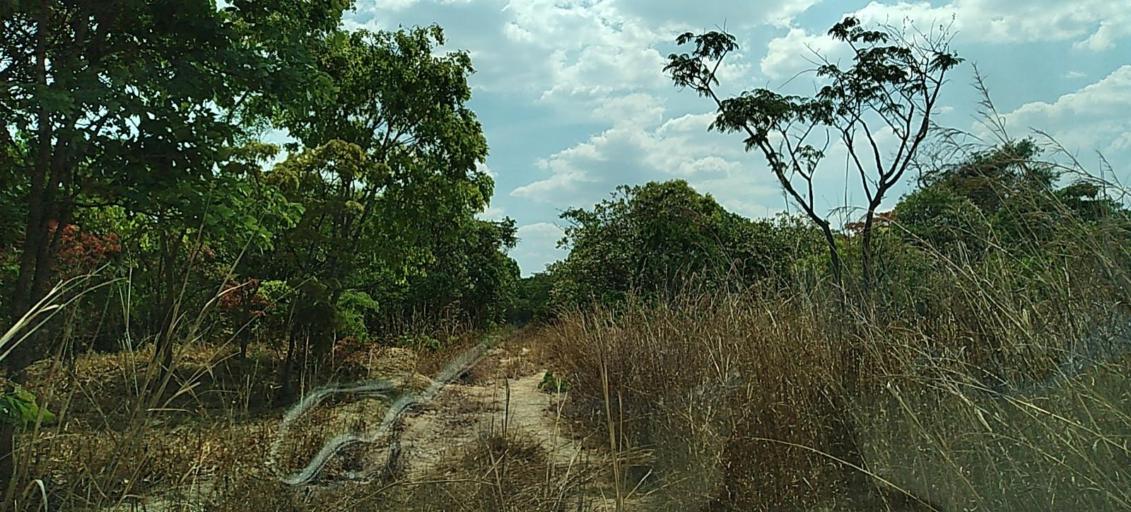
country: ZM
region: Copperbelt
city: Chililabombwe
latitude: -12.3321
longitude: 27.7630
